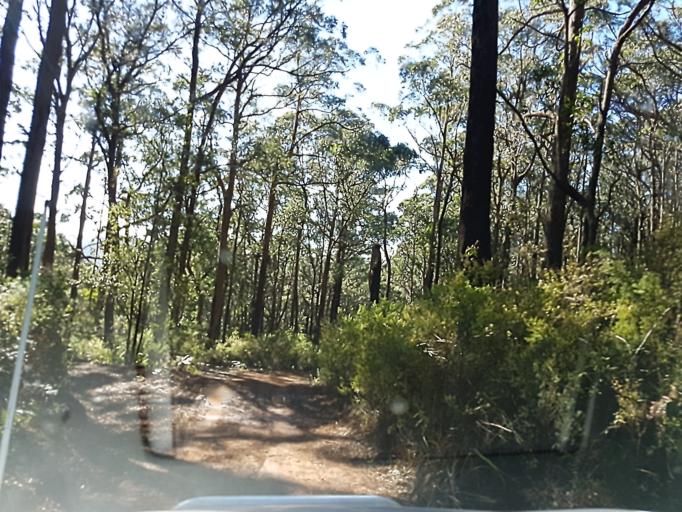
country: AU
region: Victoria
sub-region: Yarra Ranges
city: Healesville
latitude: -37.5687
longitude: 145.4984
